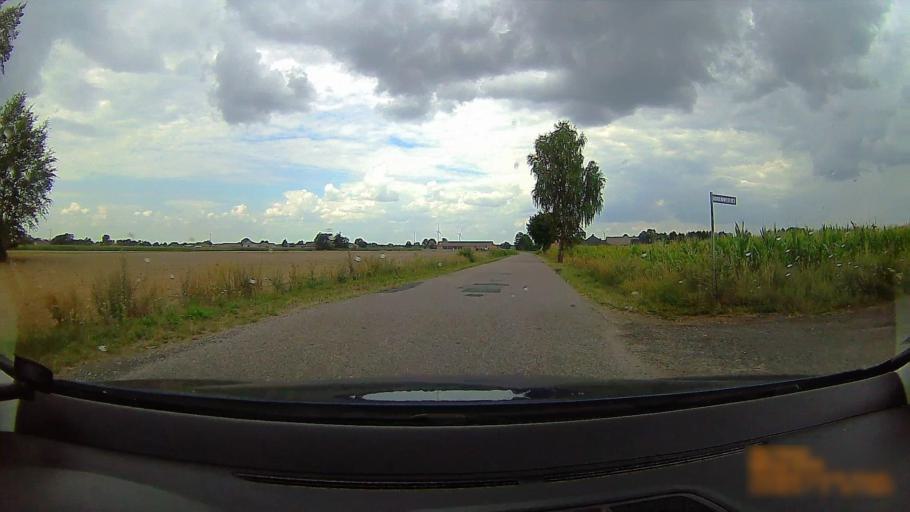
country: PL
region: Greater Poland Voivodeship
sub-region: Powiat koninski
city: Rychwal
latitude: 52.1046
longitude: 18.1912
